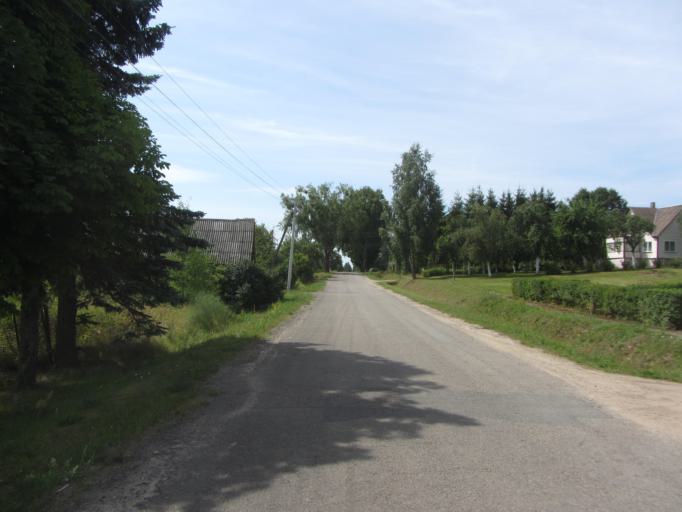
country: LT
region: Alytaus apskritis
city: Druskininkai
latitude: 54.1092
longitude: 24.1144
